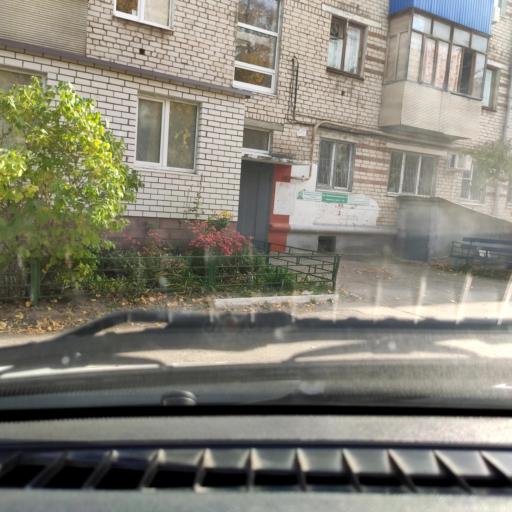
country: RU
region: Samara
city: Zhigulevsk
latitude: 53.4768
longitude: 49.4591
